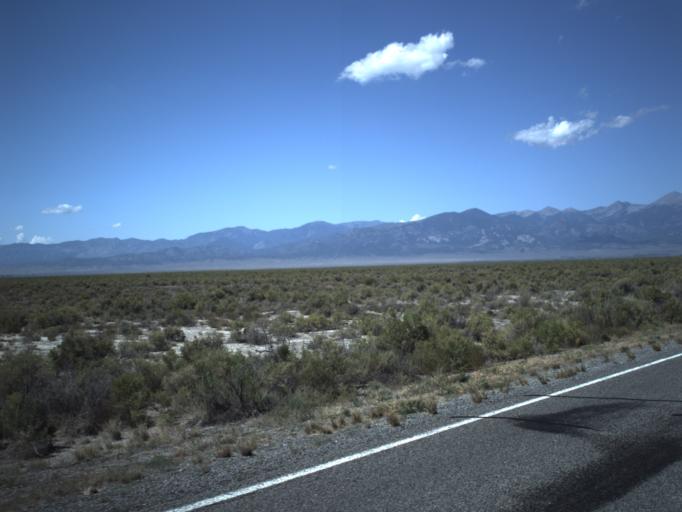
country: US
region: Nevada
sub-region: White Pine County
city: McGill
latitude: 39.0474
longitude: -113.9217
